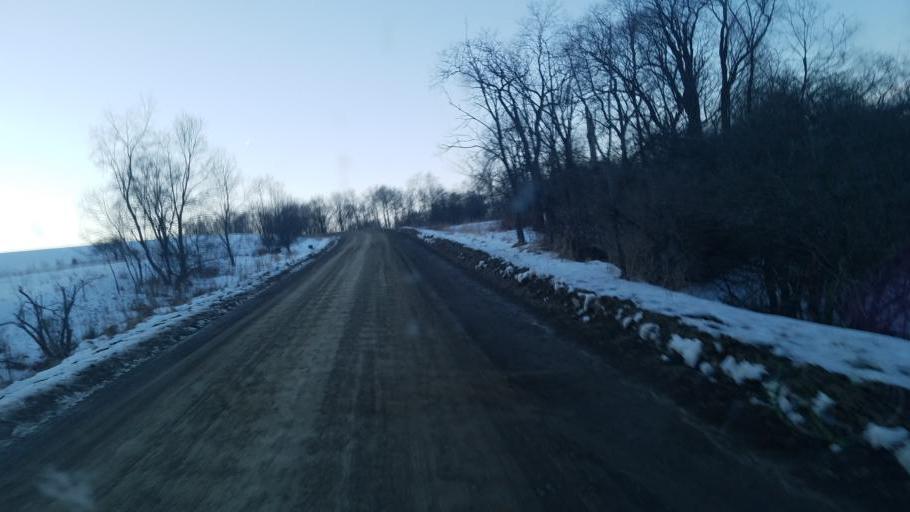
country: US
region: New York
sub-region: Allegany County
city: Andover
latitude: 42.0078
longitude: -77.7240
